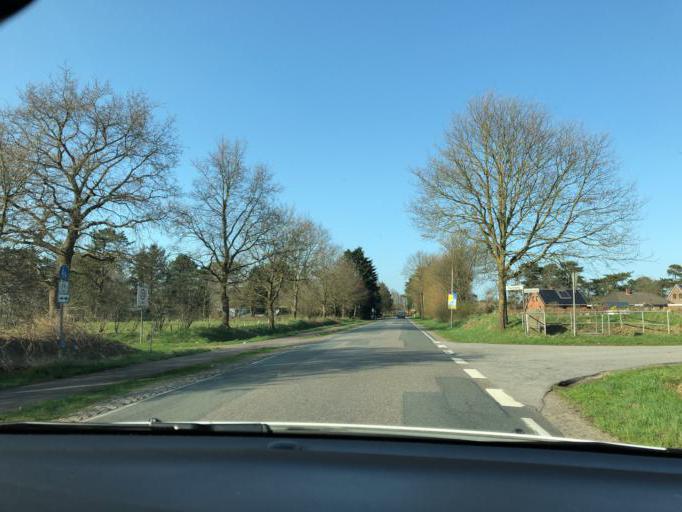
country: DE
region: Schleswig-Holstein
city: Bargum
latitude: 54.6878
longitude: 8.9632
